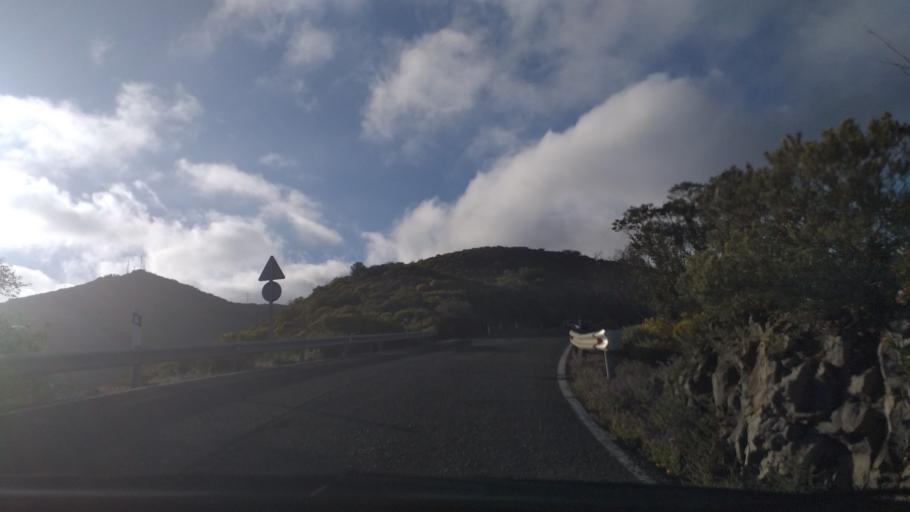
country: ES
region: Canary Islands
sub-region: Provincia de Las Palmas
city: Valsequillo de Gran Canaria
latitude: 27.9557
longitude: -15.4941
